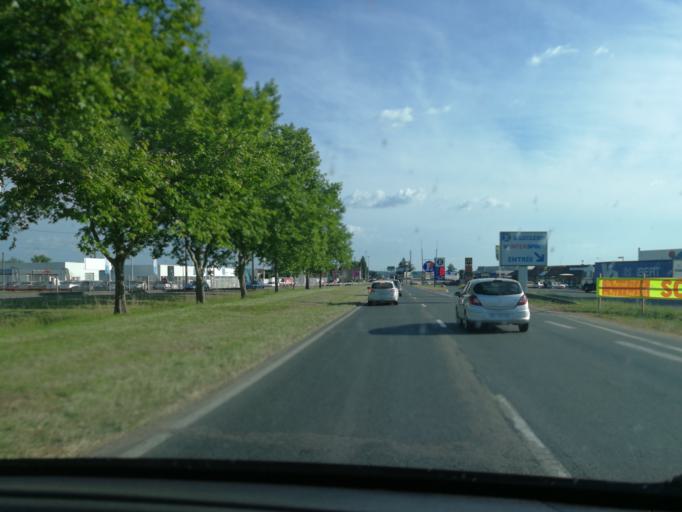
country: FR
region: Midi-Pyrenees
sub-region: Departement du Tarn
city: Albi
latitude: 43.9559
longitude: 2.1562
